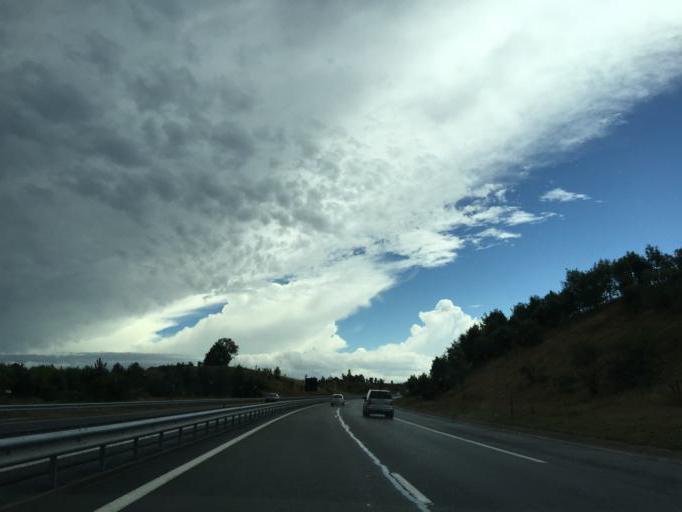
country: FR
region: Midi-Pyrenees
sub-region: Departement de l'Aveyron
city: Severac-le-Chateau
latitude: 44.3126
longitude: 3.1012
